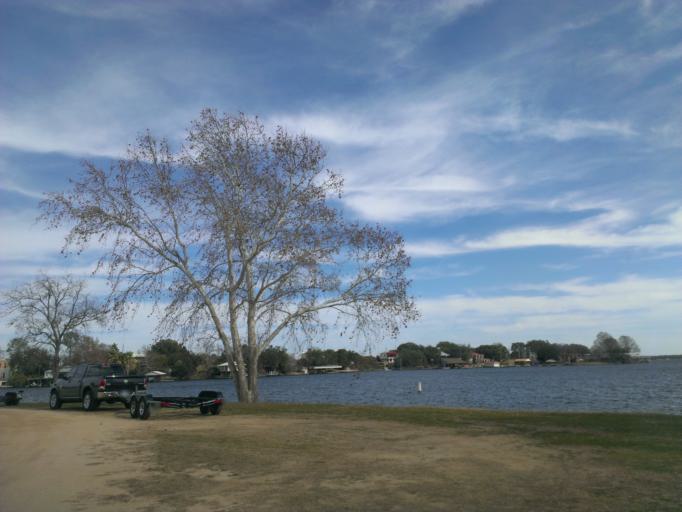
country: US
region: Texas
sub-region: Burnet County
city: Granite Shoals
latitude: 30.5760
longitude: -98.3855
